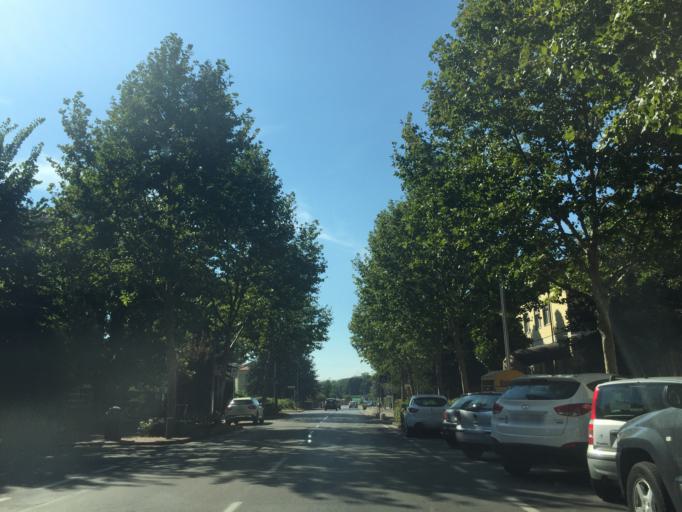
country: IT
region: Tuscany
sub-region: Provincia di Lucca
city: Lucca
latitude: 43.8494
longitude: 10.5045
